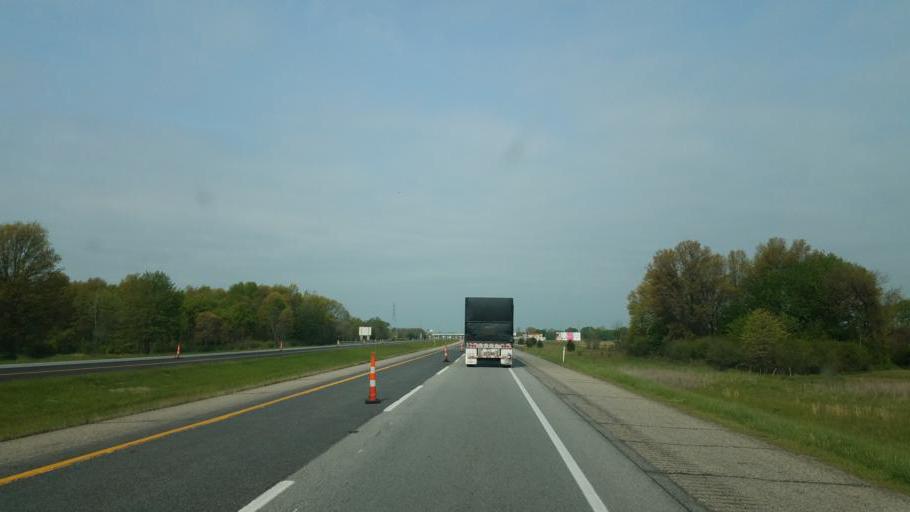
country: US
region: Indiana
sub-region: Elkhart County
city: Simonton Lake
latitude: 41.7309
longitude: -85.9531
